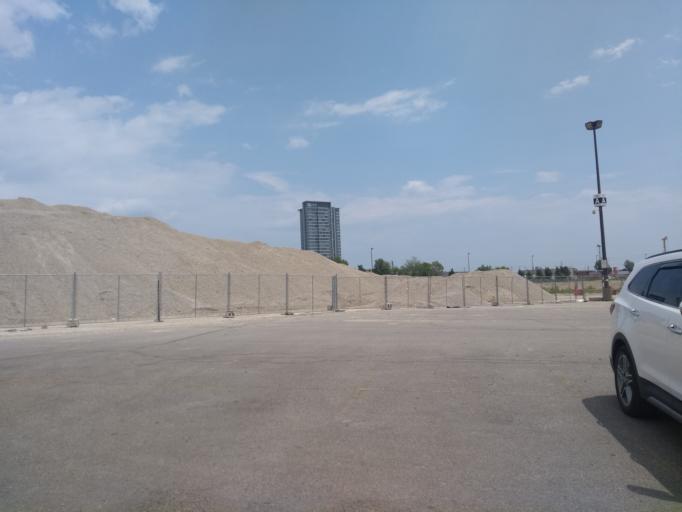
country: CA
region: Ontario
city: Markham
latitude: 43.8273
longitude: -79.3059
